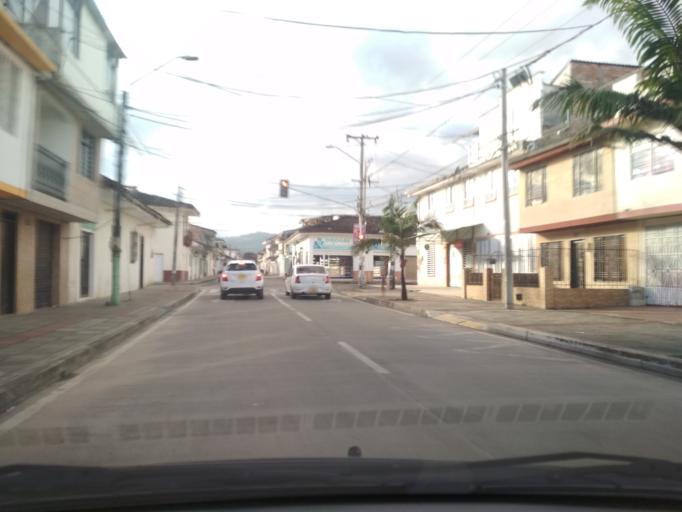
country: CO
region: Cauca
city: Popayan
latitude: 2.4418
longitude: -76.6128
